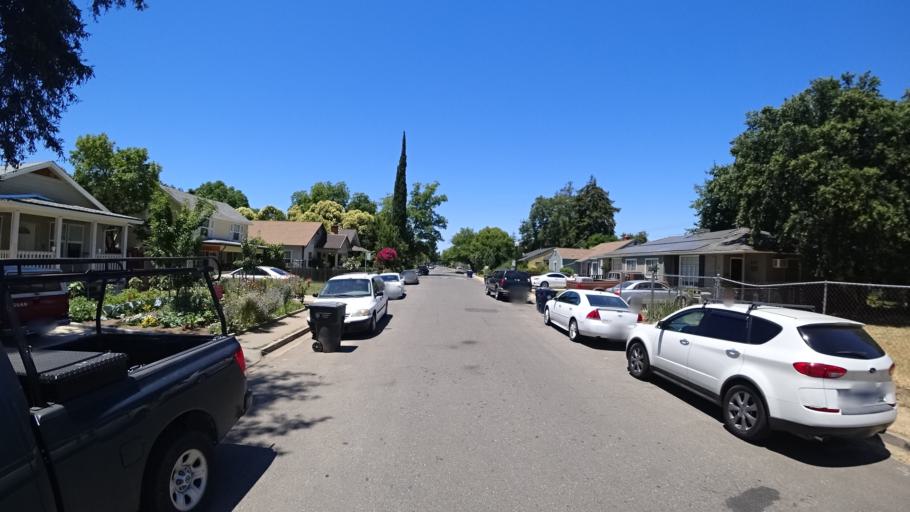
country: US
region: California
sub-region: Sacramento County
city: Sacramento
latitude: 38.5537
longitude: -121.4633
